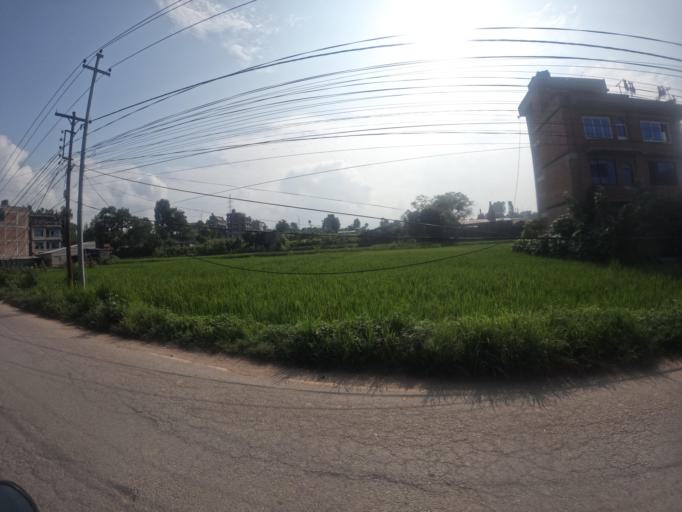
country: NP
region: Central Region
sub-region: Bagmati Zone
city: Bhaktapur
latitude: 27.6821
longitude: 85.4367
